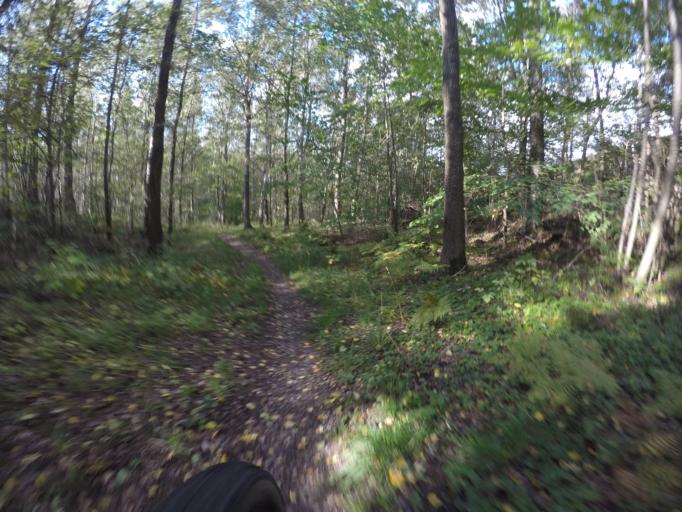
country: SE
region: Vaestmanland
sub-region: Kopings Kommun
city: Koping
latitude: 59.5072
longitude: 16.0202
